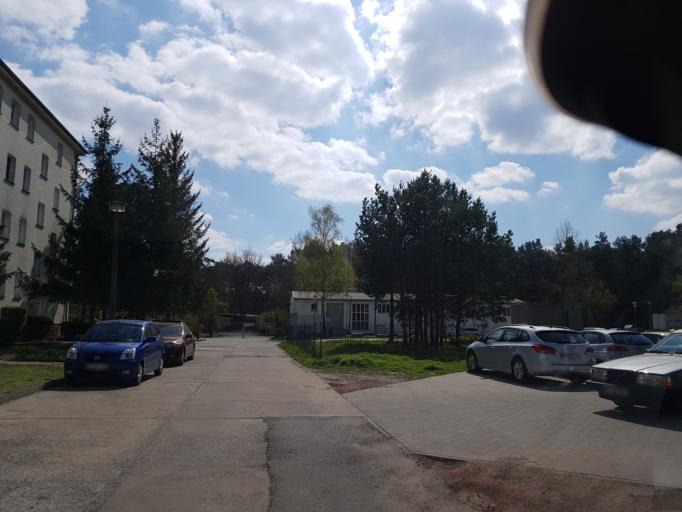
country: DE
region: Brandenburg
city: Bruck
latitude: 52.1872
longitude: 12.7543
